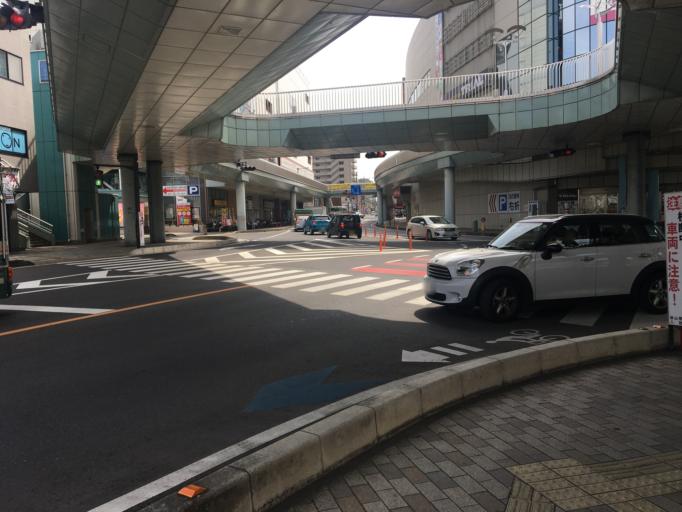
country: JP
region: Saitama
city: Sayama
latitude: 35.8368
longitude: 139.3876
